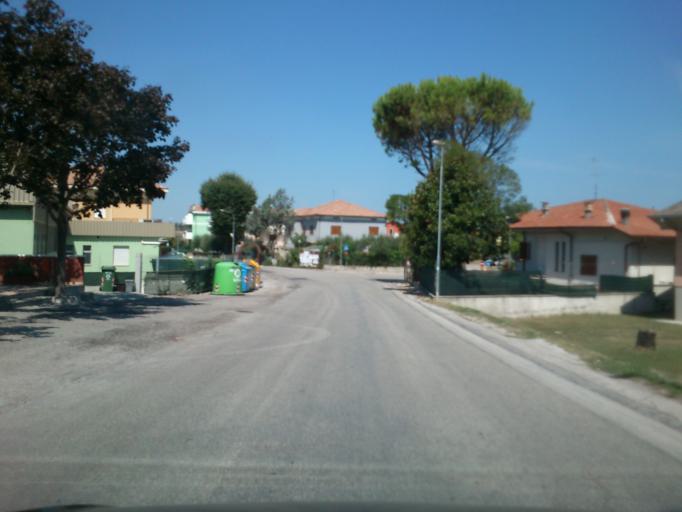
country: IT
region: The Marches
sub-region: Provincia di Pesaro e Urbino
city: Lucrezia
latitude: 43.7678
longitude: 12.9513
